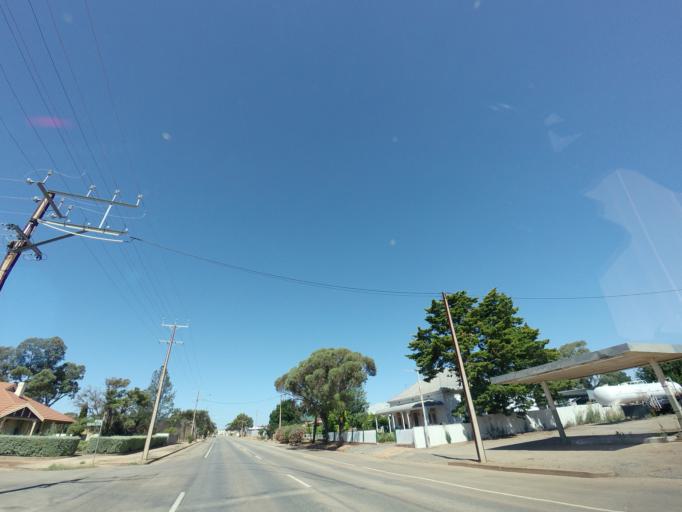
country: AU
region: South Australia
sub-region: Peterborough
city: Peterborough
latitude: -32.9727
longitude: 138.8438
